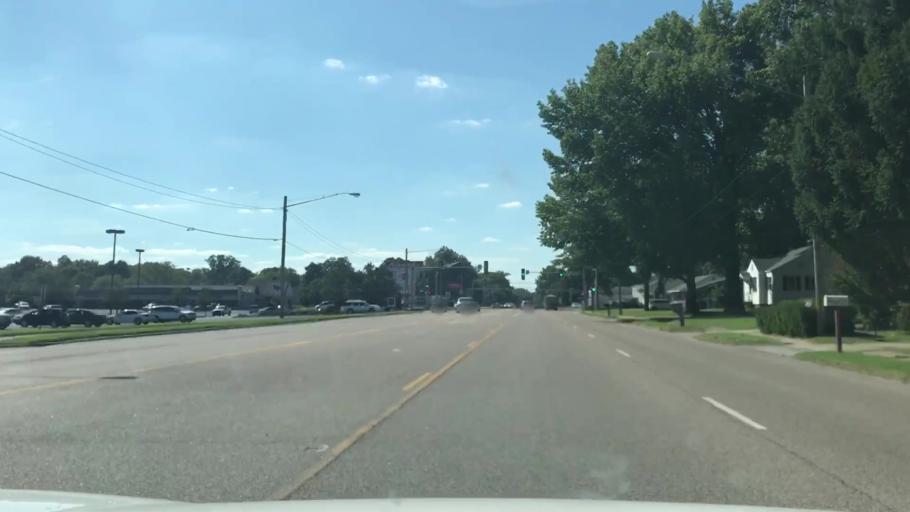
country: US
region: Illinois
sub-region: Saint Clair County
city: Swansea
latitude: 38.5417
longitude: -90.0334
